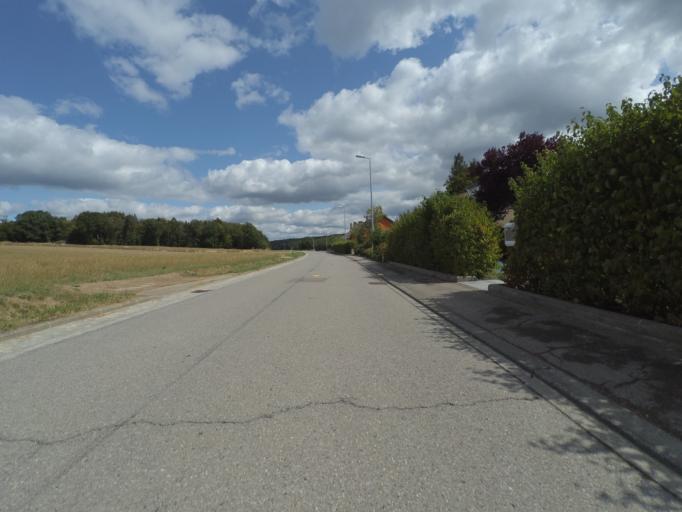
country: LU
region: Grevenmacher
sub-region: Canton de Grevenmacher
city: Flaxweiler
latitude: 49.6694
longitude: 6.3466
